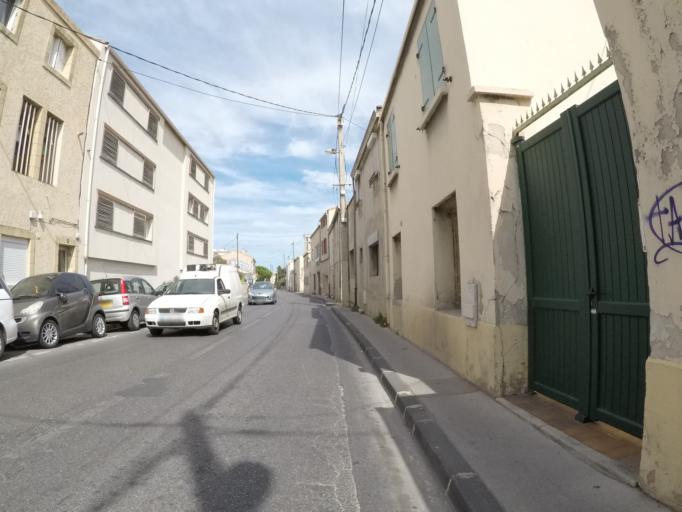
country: FR
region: Provence-Alpes-Cote d'Azur
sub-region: Departement des Bouches-du-Rhone
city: Marseille 08
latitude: 43.2369
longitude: 5.3630
